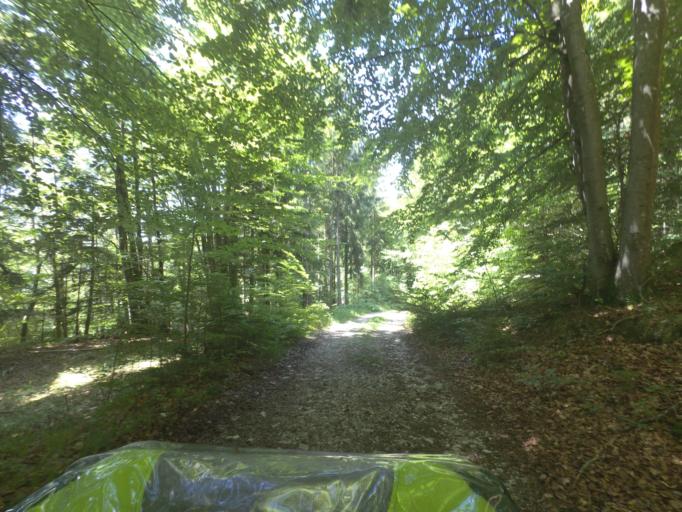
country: AT
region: Salzburg
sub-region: Politischer Bezirk Hallein
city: Oberalm
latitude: 47.7132
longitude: 13.1139
